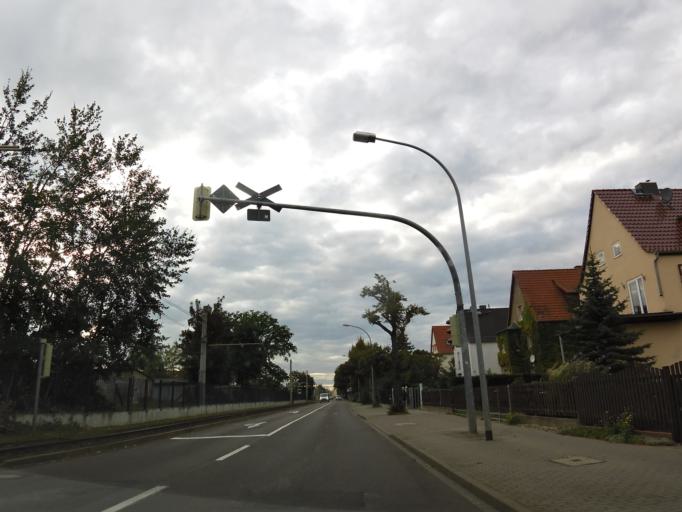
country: DE
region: Saxony
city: Schkeuditz
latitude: 51.3608
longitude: 12.2821
